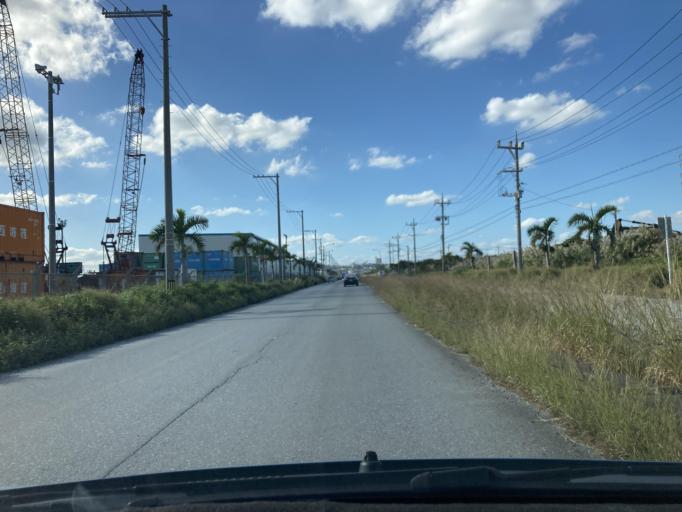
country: JP
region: Okinawa
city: Katsuren-haebaru
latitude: 26.3257
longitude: 127.8520
